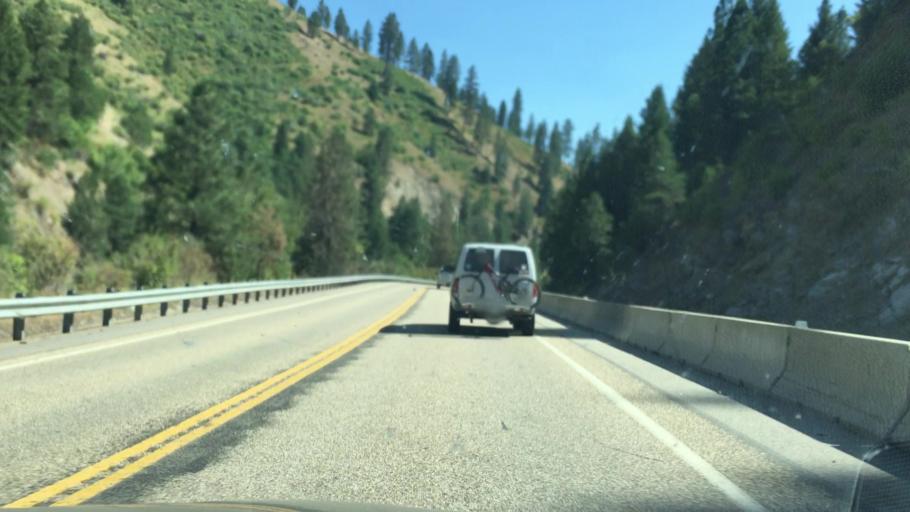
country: US
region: Idaho
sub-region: Valley County
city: Cascade
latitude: 44.1254
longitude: -116.1116
